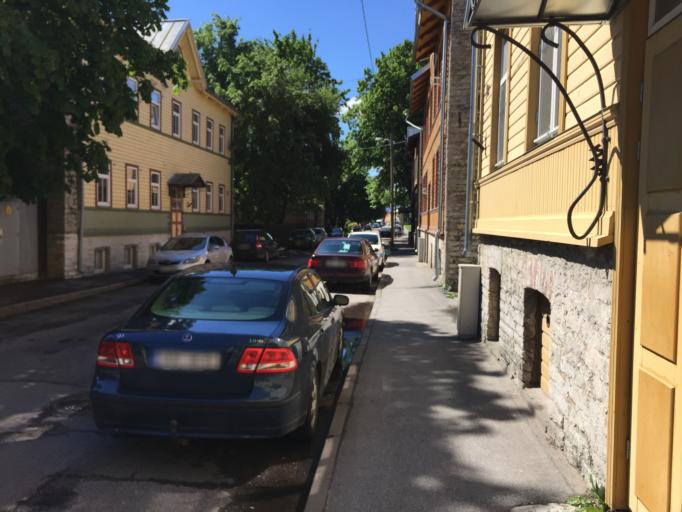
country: EE
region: Harju
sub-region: Tallinna linn
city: Tallinn
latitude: 59.4455
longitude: 24.7326
